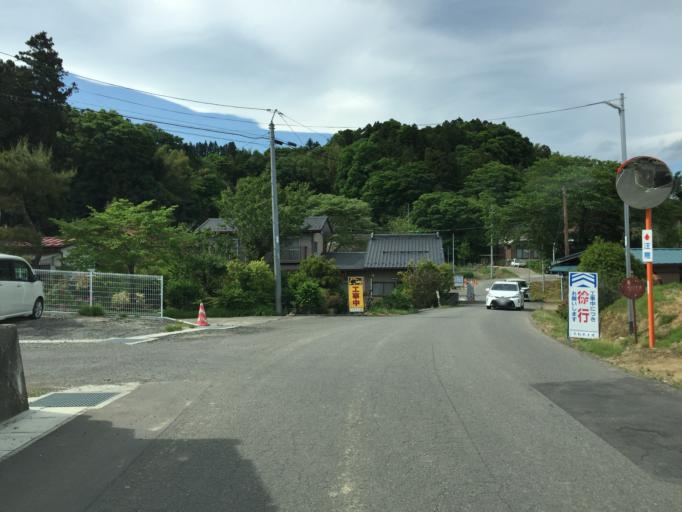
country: JP
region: Fukushima
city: Nihommatsu
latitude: 37.6364
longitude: 140.5218
